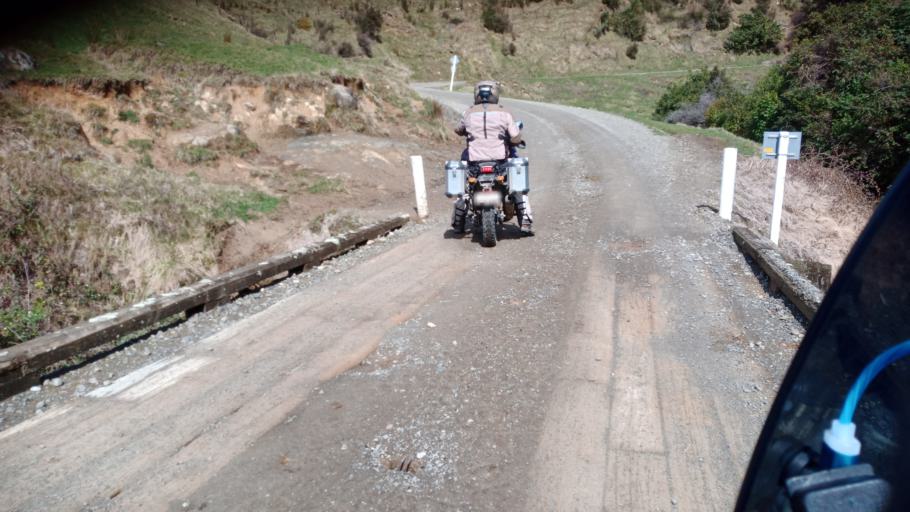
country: NZ
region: Hawke's Bay
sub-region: Wairoa District
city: Wairoa
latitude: -38.7351
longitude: 177.3007
